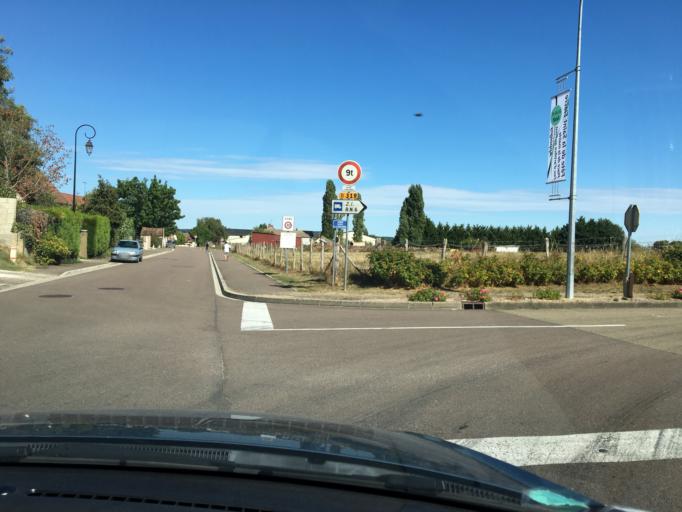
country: FR
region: Bourgogne
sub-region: Departement de l'Yonne
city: Appoigny
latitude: 47.8749
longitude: 3.5189
